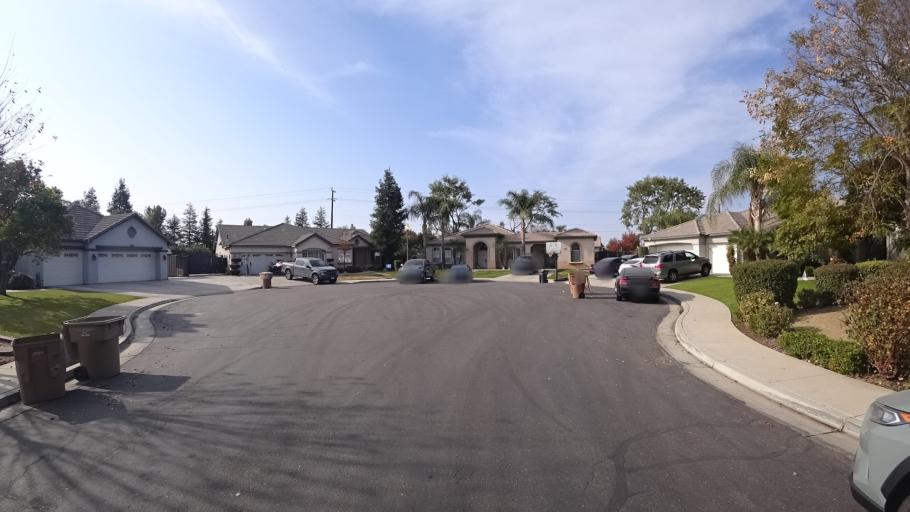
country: US
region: California
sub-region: Kern County
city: Greenacres
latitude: 35.4158
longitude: -119.1090
